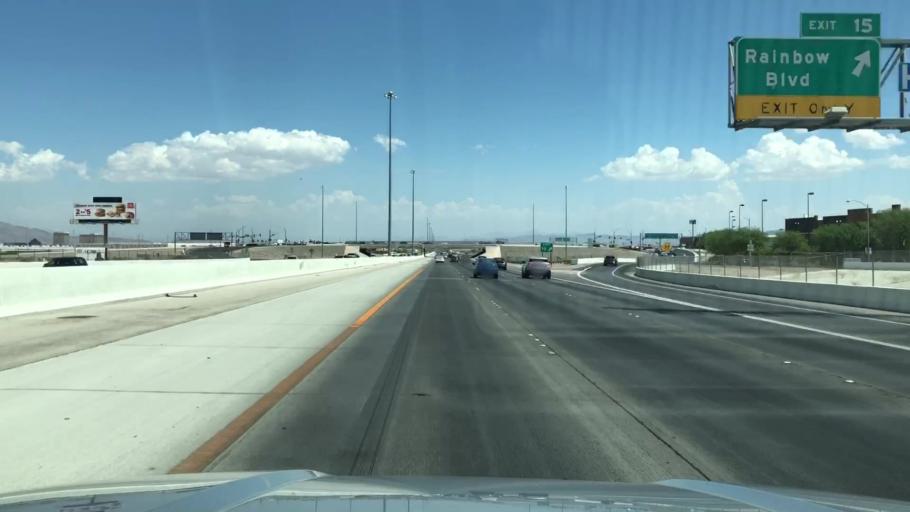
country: US
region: Nevada
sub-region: Clark County
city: Enterprise
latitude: 36.0664
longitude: -115.2482
